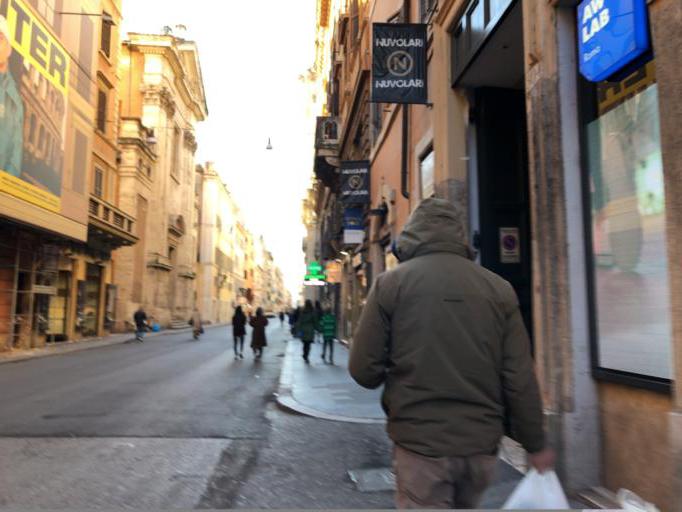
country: VA
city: Vatican City
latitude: 41.9084
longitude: 12.4773
